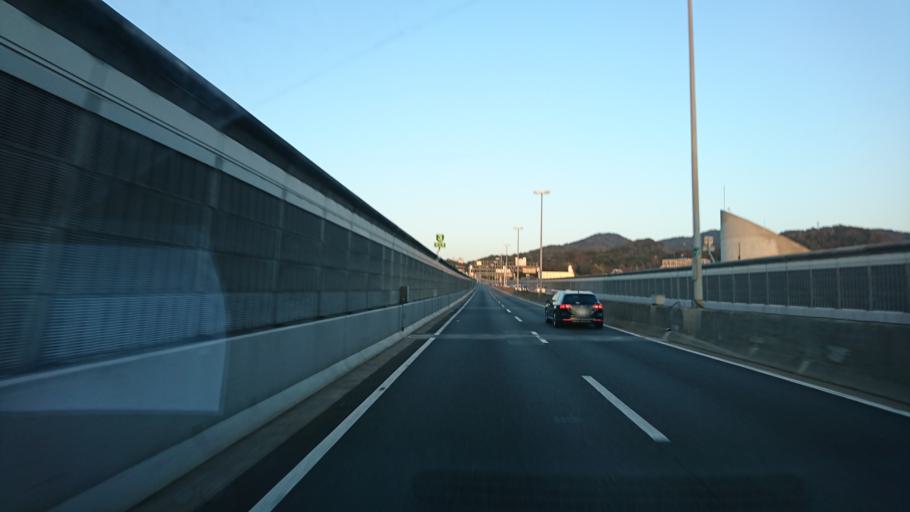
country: JP
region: Hyogo
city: Kobe
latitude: 34.6506
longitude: 135.1284
